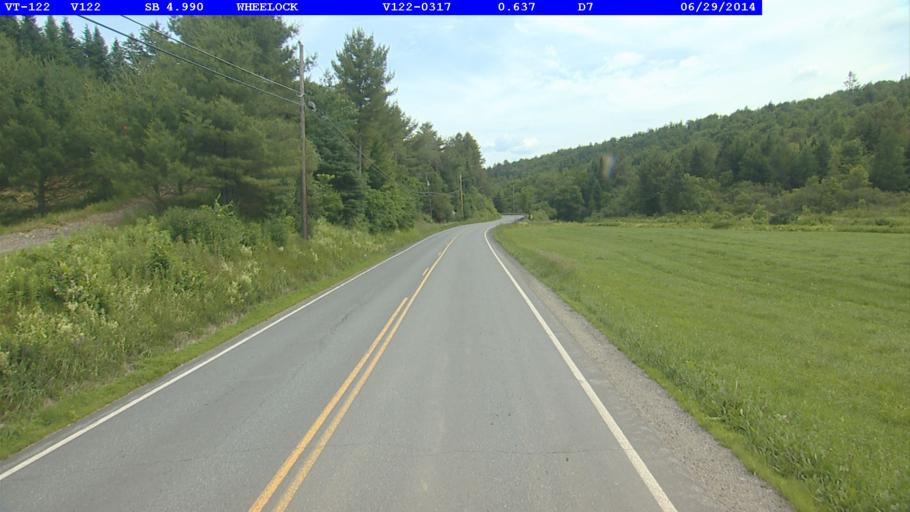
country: US
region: Vermont
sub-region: Caledonia County
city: Lyndonville
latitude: 44.5828
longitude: -72.0755
